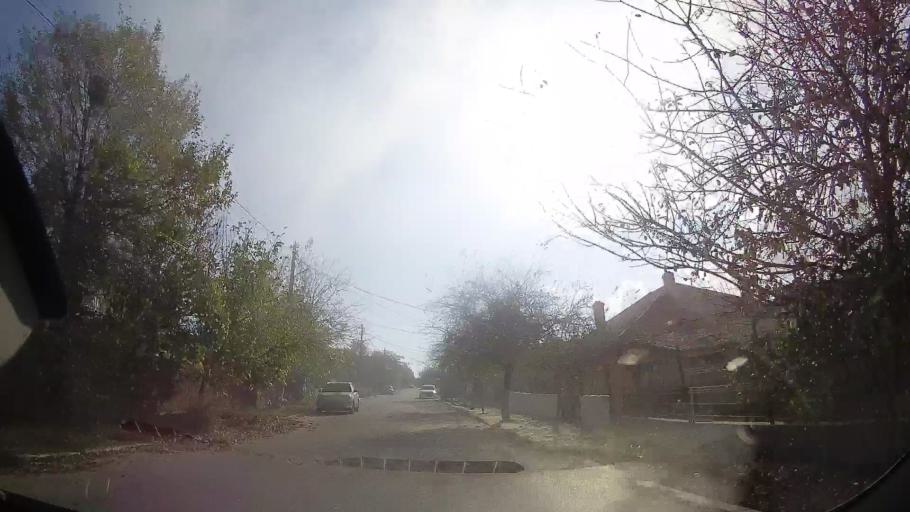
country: RO
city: Eforie Sud
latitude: 44.0112
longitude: 28.6443
